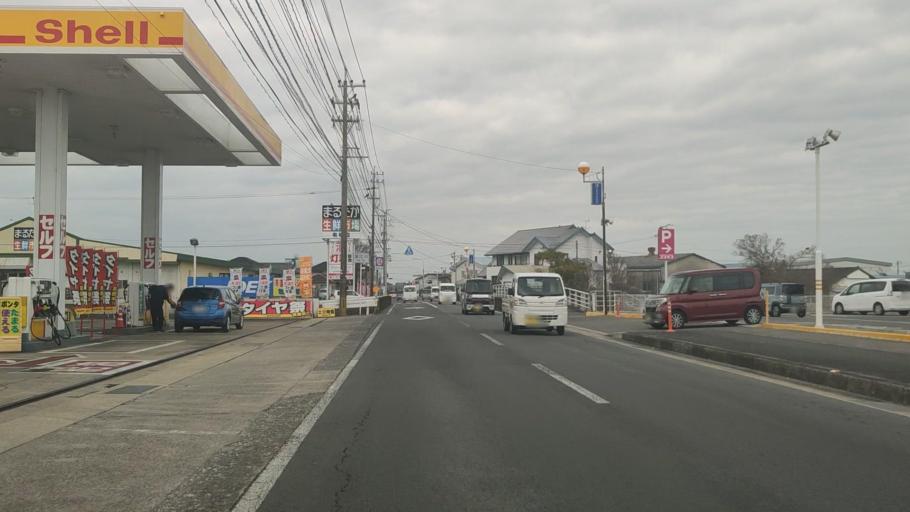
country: JP
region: Nagasaki
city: Shimabara
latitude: 32.8607
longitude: 130.3263
